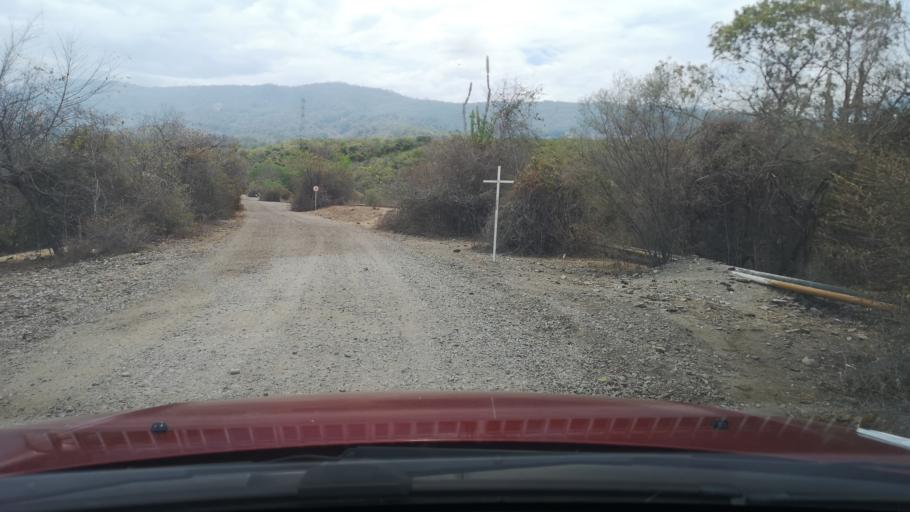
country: CO
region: Huila
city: Neiva
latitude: 2.9576
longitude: -75.3394
